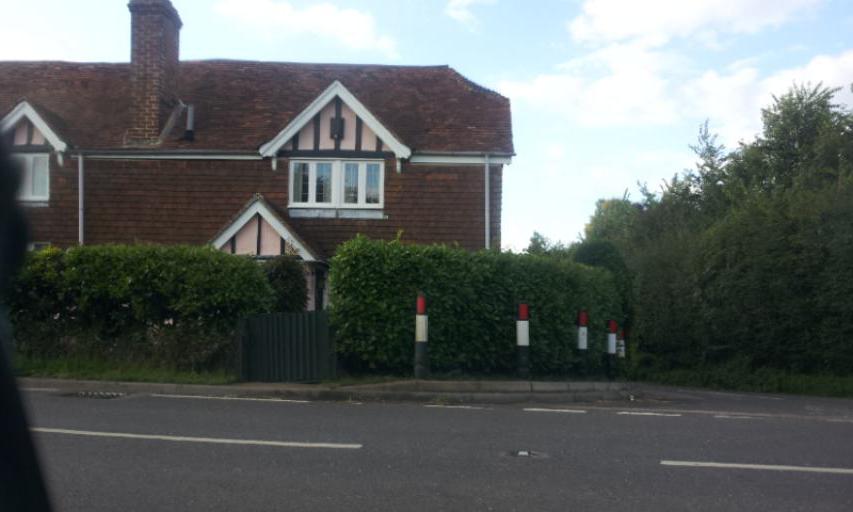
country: GB
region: England
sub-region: Kent
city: Maidstone
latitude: 51.2264
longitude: 0.5599
